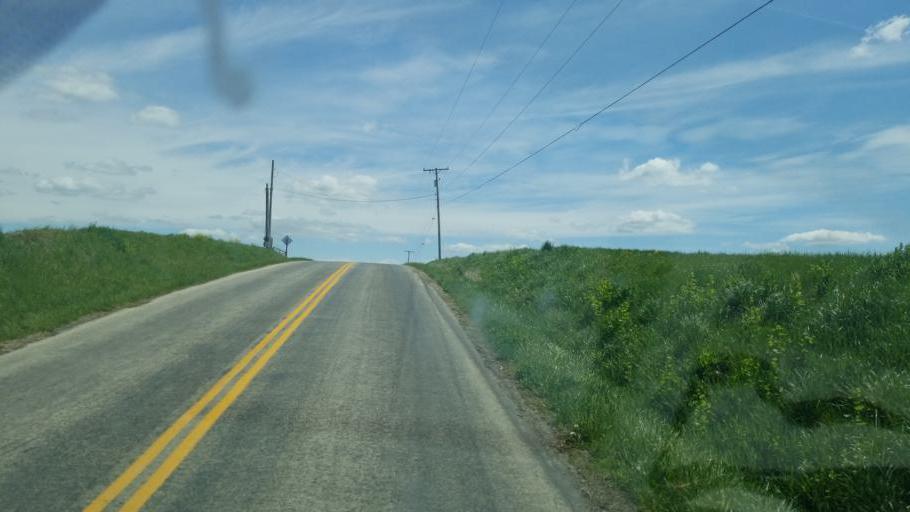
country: US
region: Ohio
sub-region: Ashland County
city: Loudonville
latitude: 40.7590
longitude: -82.1530
